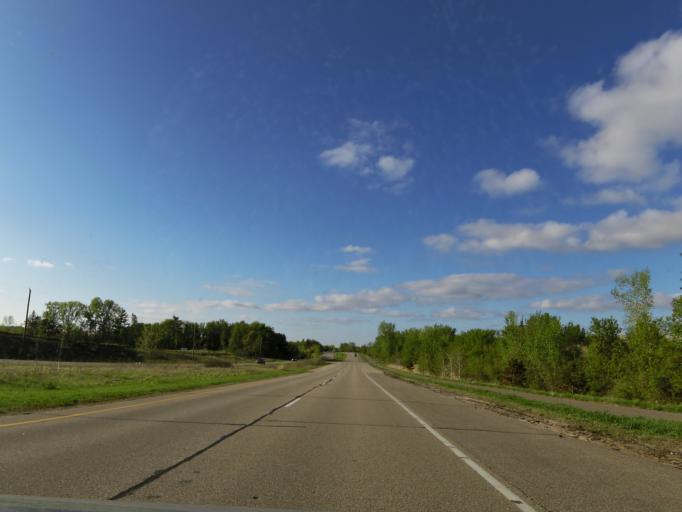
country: US
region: Minnesota
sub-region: Washington County
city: Lake Elmo
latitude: 44.9576
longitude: -92.9030
